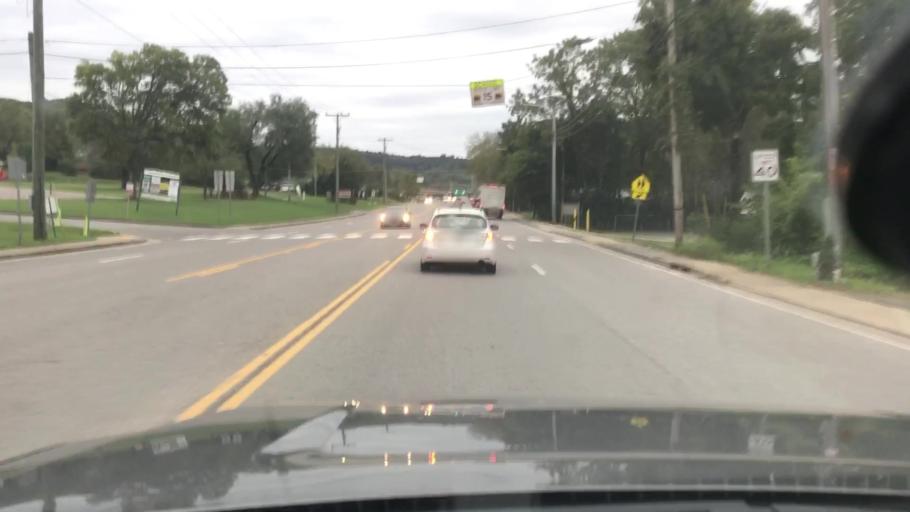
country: US
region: Tennessee
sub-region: Davidson County
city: Belle Meade
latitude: 36.1161
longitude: -86.9232
